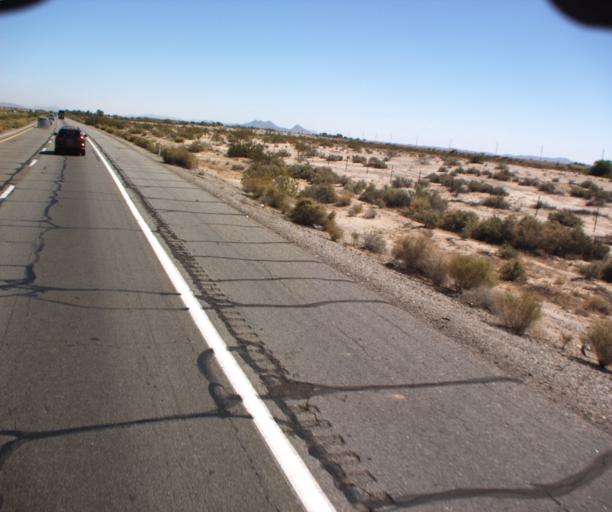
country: US
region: Arizona
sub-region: Yuma County
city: Wellton
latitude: 32.6493
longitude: -114.1946
